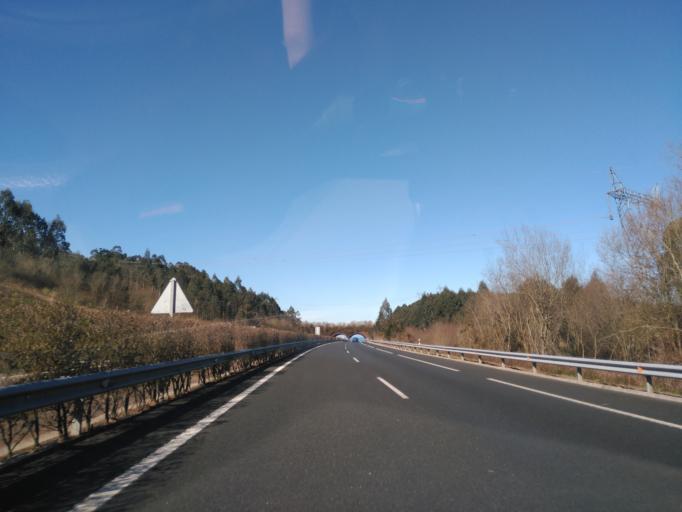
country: ES
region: Cantabria
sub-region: Provincia de Cantabria
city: Comillas
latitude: 43.3253
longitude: -4.2979
